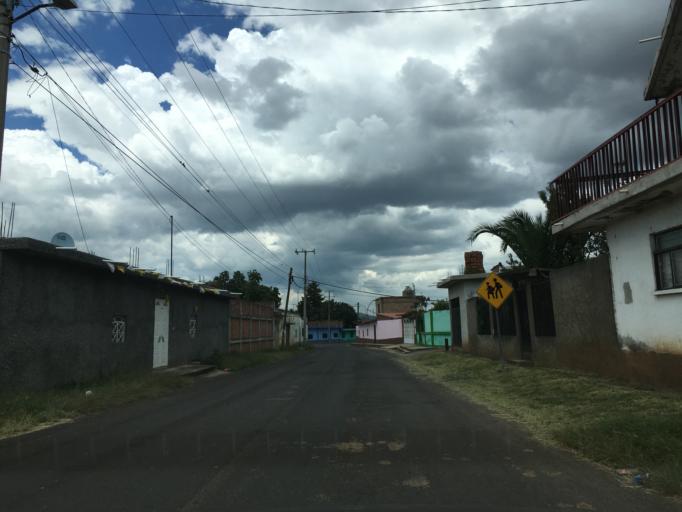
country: MX
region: Michoacan
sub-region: Jimenez
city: Copandaro (Copandaro del Cuatro)
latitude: 19.8176
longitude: -101.6803
